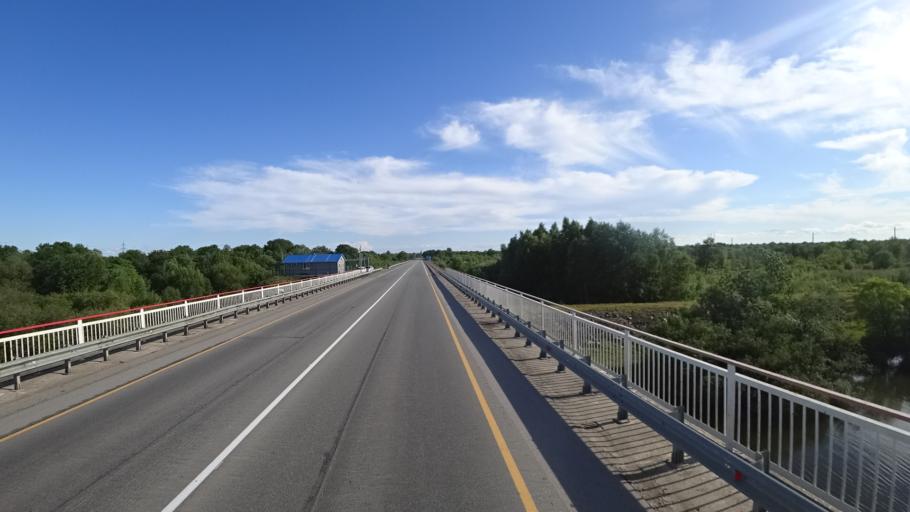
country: RU
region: Khabarovsk Krai
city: Khor
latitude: 47.8636
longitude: 134.9637
